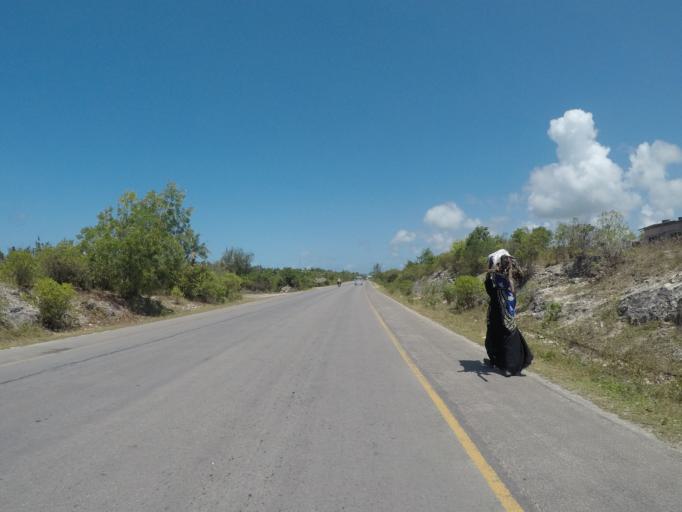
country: TZ
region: Zanzibar Central/South
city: Nganane
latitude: -6.3069
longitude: 39.5400
